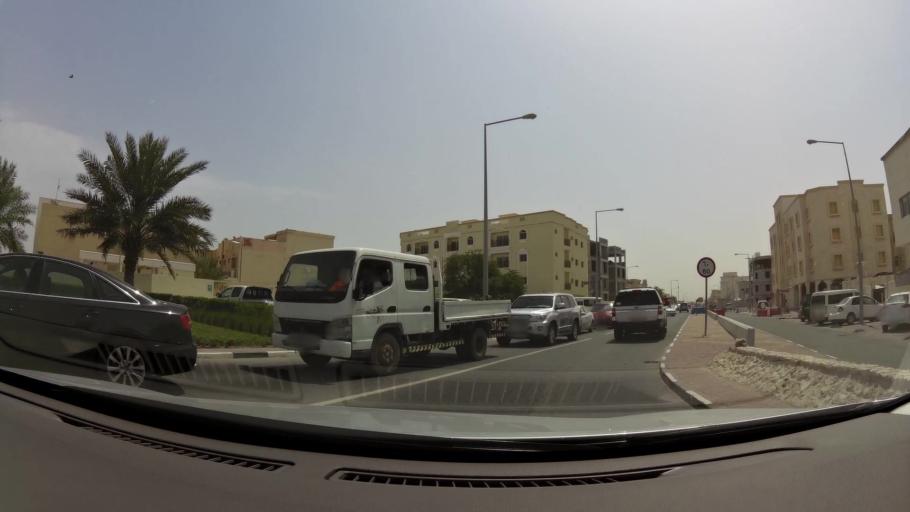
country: QA
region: Baladiyat ar Rayyan
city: Ar Rayyan
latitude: 25.3220
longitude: 51.4763
